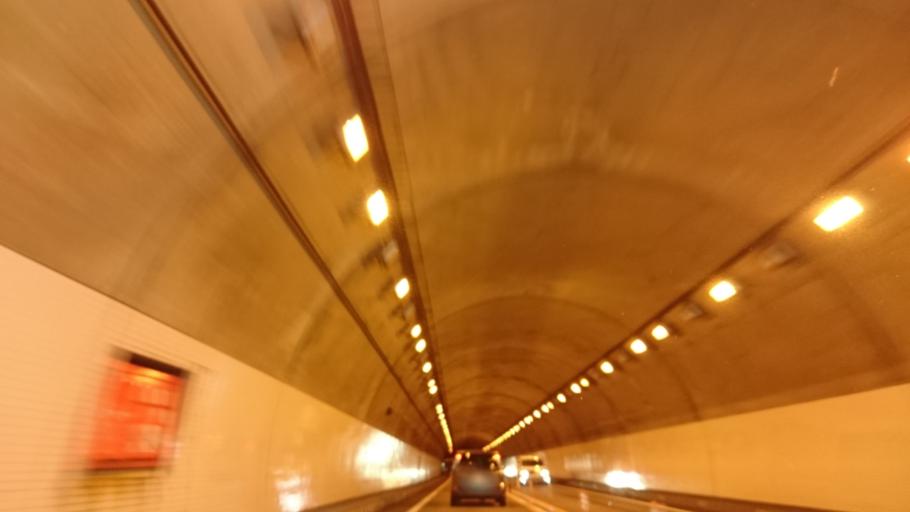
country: JP
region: Gifu
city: Takayama
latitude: 36.0274
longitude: 137.0057
